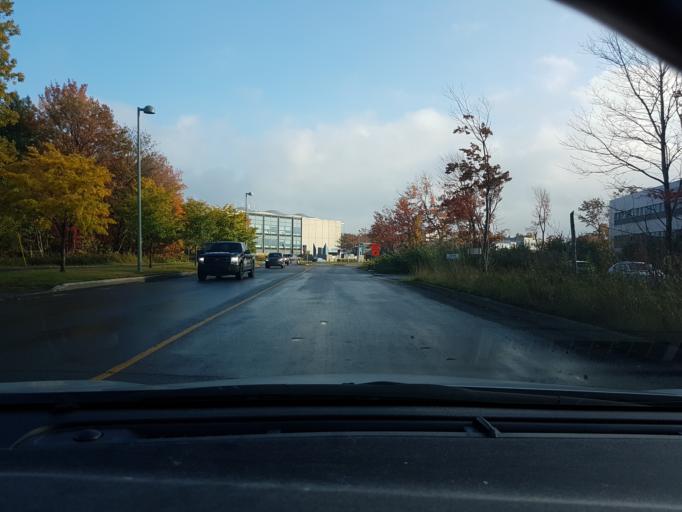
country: CA
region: Quebec
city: L'Ancienne-Lorette
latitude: 46.7975
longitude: -71.3142
